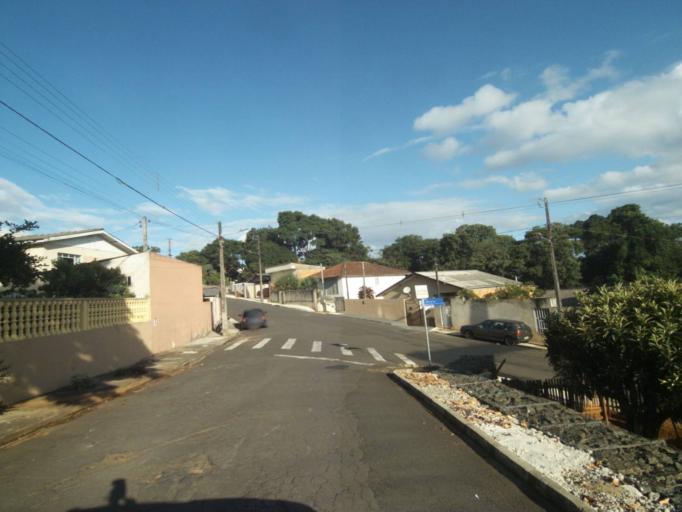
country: BR
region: Parana
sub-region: Telemaco Borba
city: Telemaco Borba
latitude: -24.3324
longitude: -50.6123
